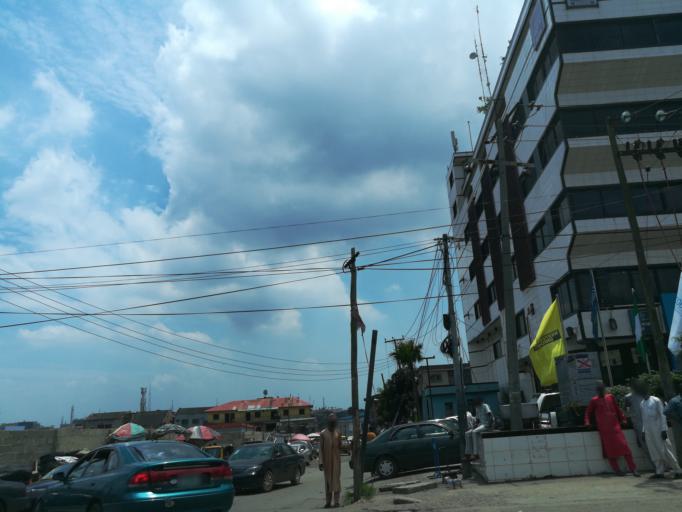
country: NG
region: Lagos
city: Ikeja
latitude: 6.6053
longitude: 3.3501
